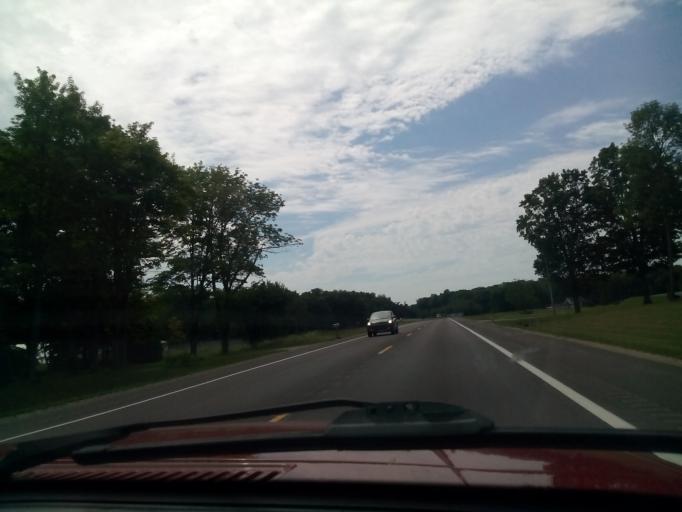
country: US
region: Michigan
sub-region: Schoolcraft County
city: Manistique
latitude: 46.0856
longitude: -85.9549
